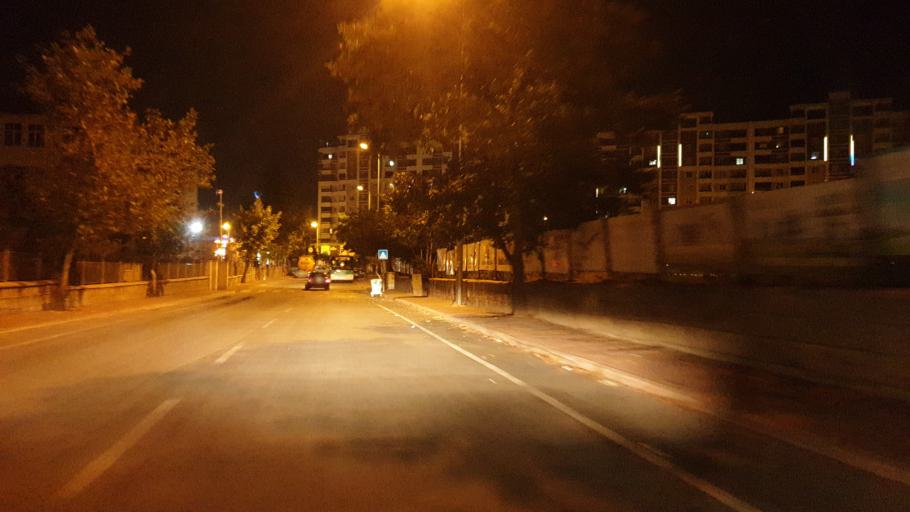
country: TR
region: Kayseri
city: Talas
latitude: 38.6936
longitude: 35.5424
